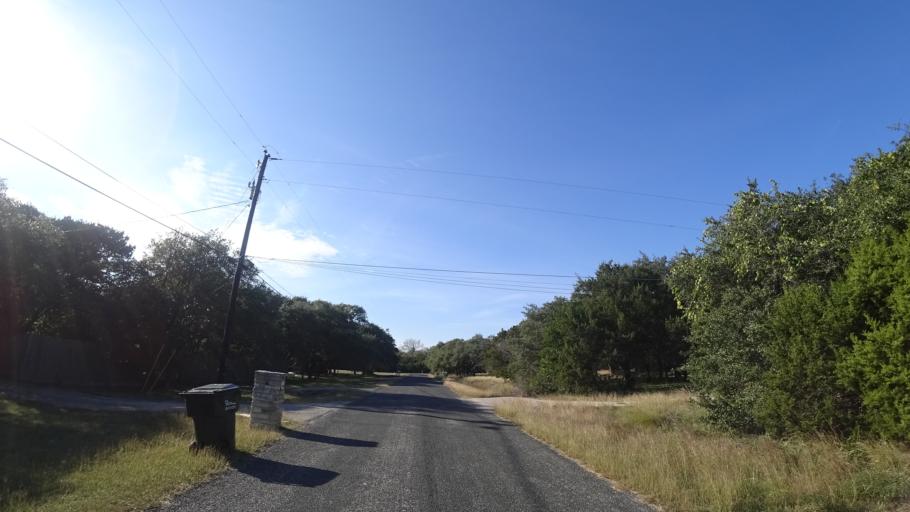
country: US
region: Texas
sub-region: Travis County
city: Barton Creek
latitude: 30.2454
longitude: -97.9121
